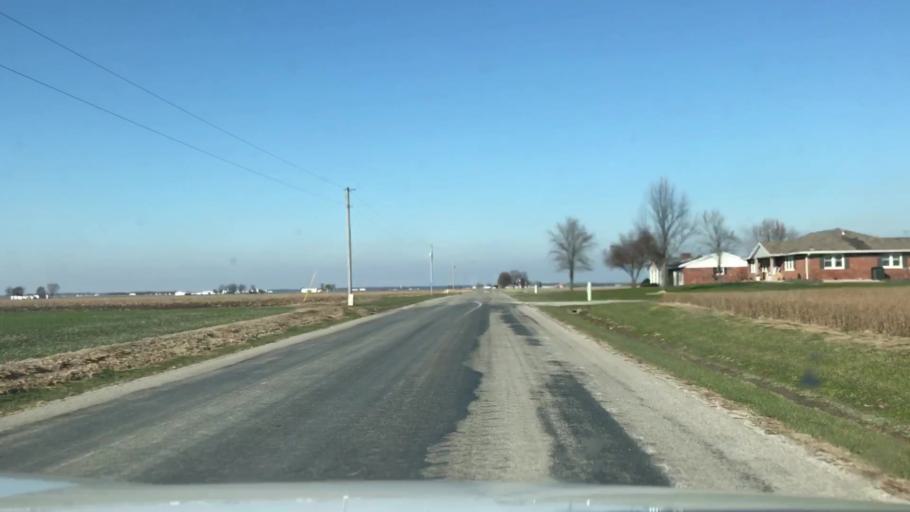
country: US
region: Illinois
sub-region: Washington County
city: Okawville
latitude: 38.4052
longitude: -89.4865
